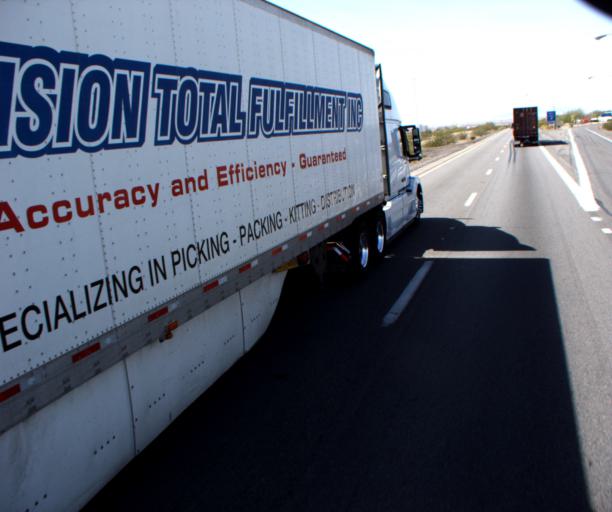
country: US
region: Arizona
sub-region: La Paz County
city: Ehrenberg
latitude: 33.6218
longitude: -114.4435
